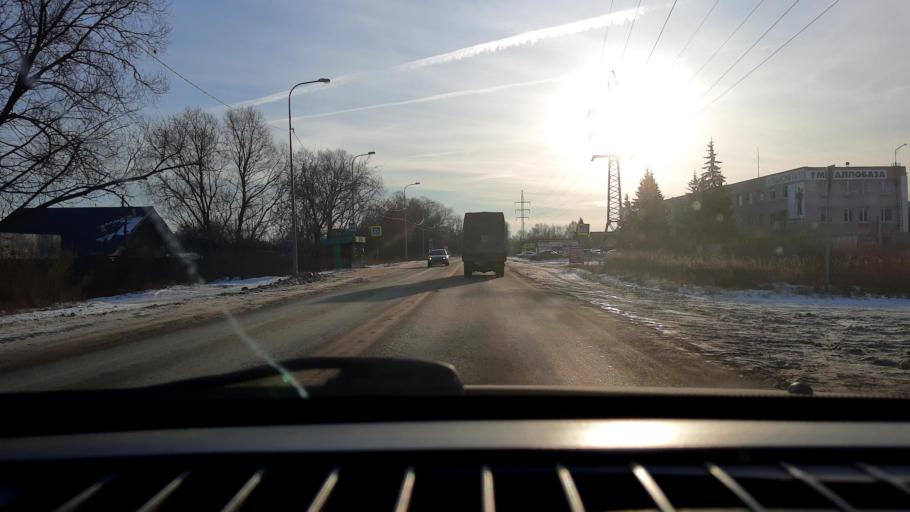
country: RU
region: Nizjnij Novgorod
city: Bor
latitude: 56.3705
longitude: 44.0662
